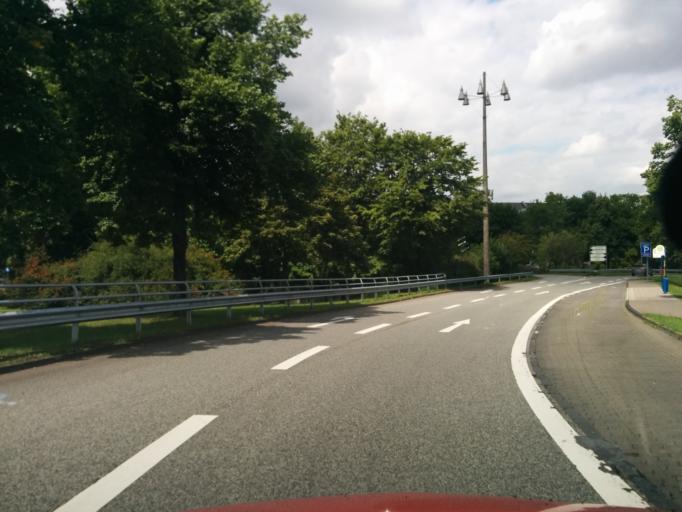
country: DE
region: Rheinland-Pfalz
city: Koblenz
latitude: 50.3543
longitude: 7.6000
